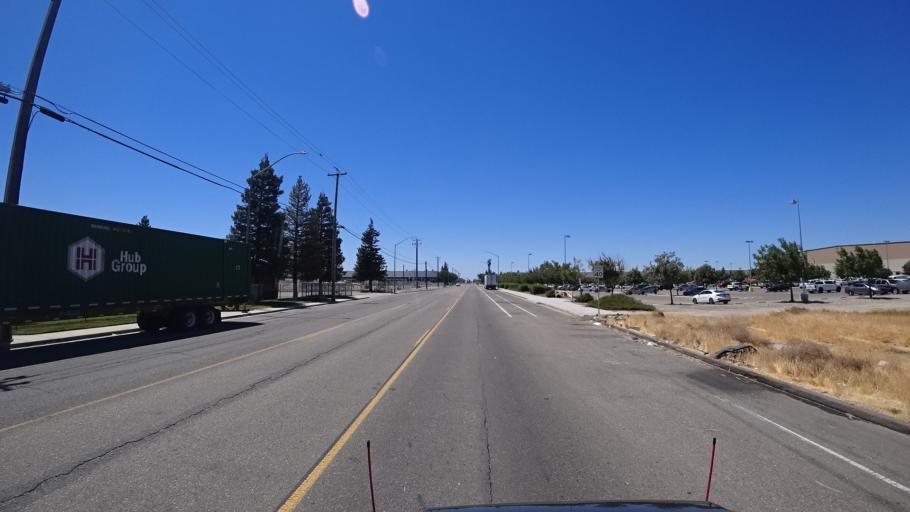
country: US
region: California
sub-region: Fresno County
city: Easton
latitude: 36.6903
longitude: -119.7728
